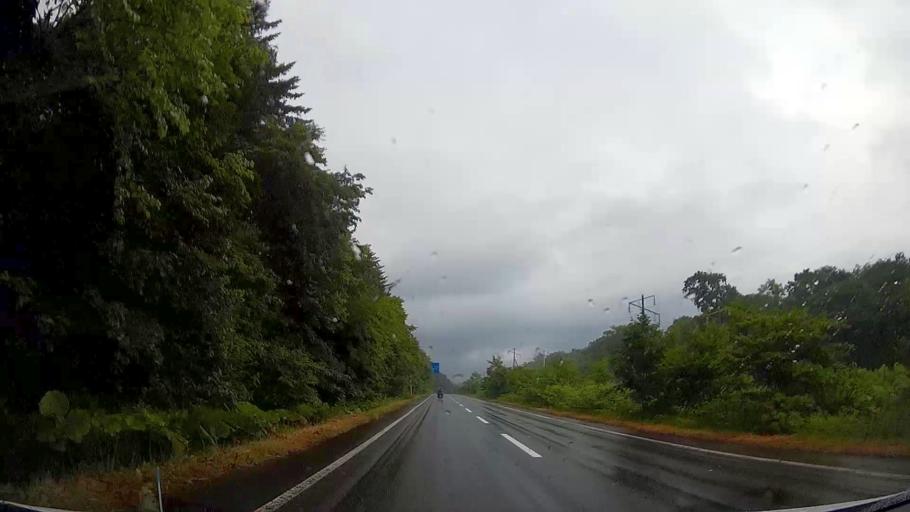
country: JP
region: Hokkaido
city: Tomakomai
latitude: 42.7604
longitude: 141.4374
